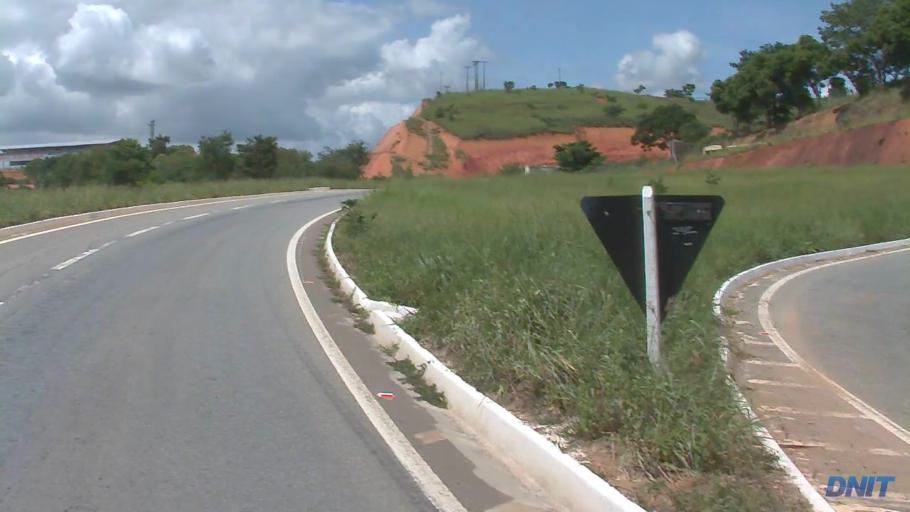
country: BR
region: Minas Gerais
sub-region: Governador Valadares
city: Governador Valadares
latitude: -18.9147
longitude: -42.0107
